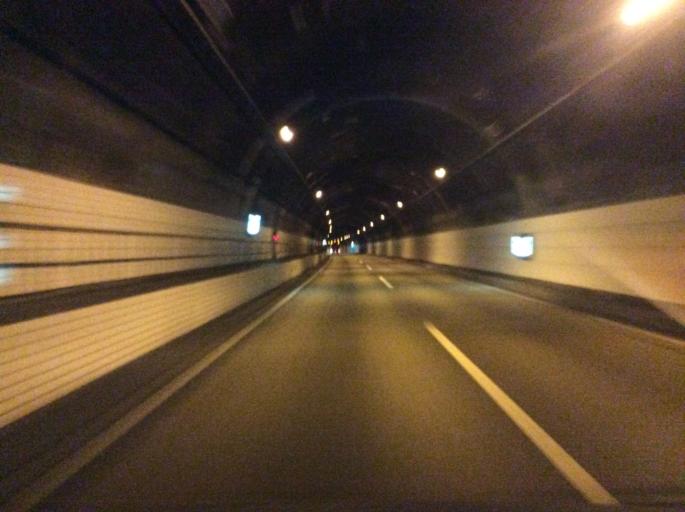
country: JP
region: Ibaraki
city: Hitachi
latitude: 36.5647
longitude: 140.6069
